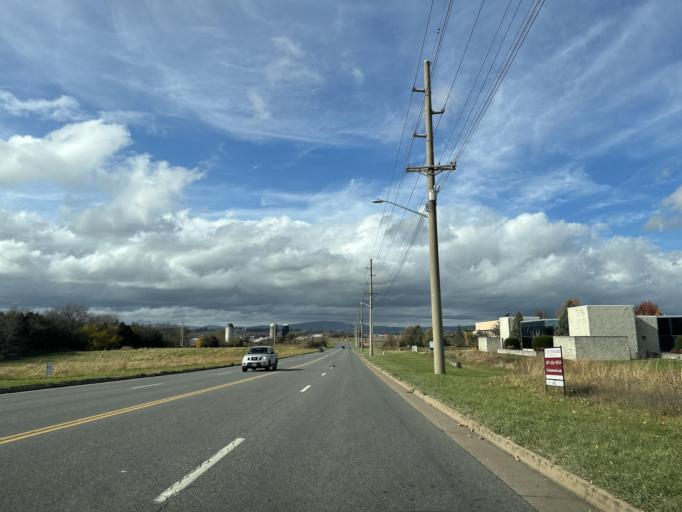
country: US
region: Virginia
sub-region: City of Harrisonburg
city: Harrisonburg
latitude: 38.4644
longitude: -78.8516
